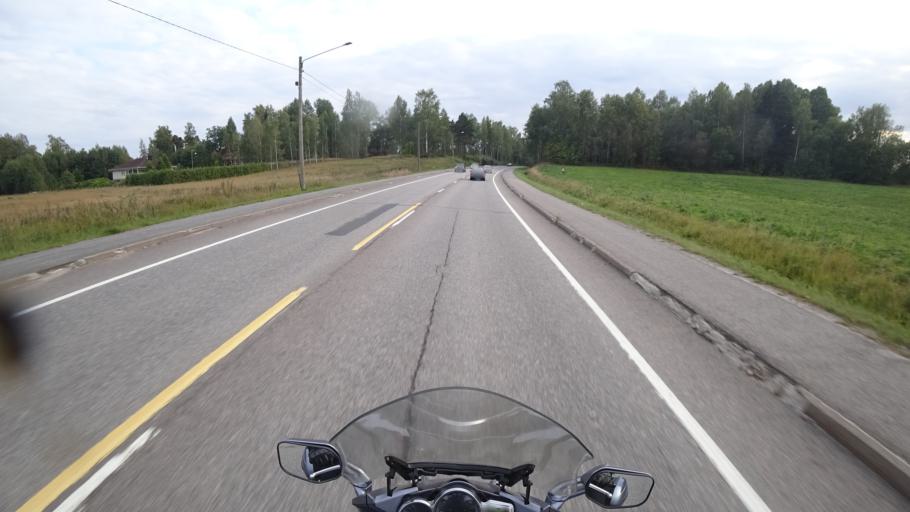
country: FI
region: Uusimaa
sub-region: Raaseporin
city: Karis
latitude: 60.0801
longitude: 23.6619
